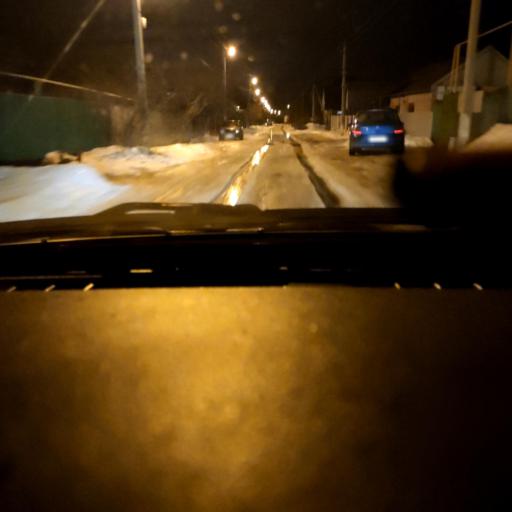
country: RU
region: Voronezj
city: Podgornoye
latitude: 51.7418
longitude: 39.1701
